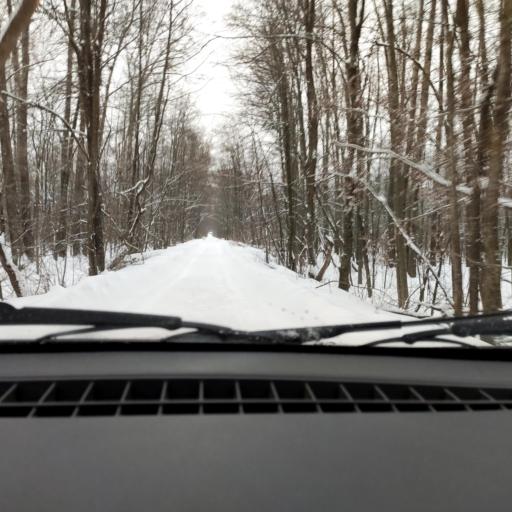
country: RU
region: Bashkortostan
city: Ufa
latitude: 54.7941
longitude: 56.1086
